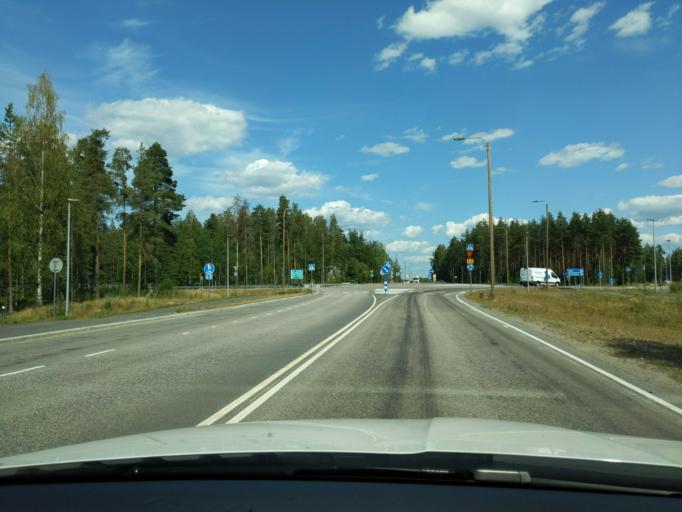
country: FI
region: Paijanne Tavastia
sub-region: Lahti
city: Heinola
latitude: 61.1077
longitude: 25.9340
